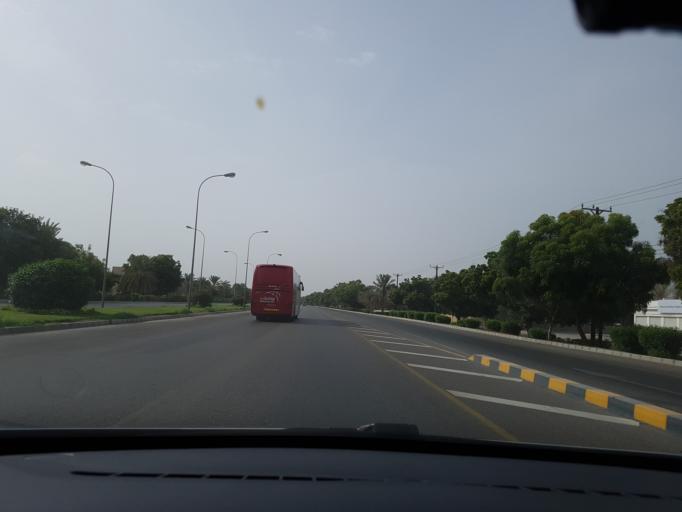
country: OM
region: Al Batinah
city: Al Sohar
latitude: 24.3704
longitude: 56.7050
